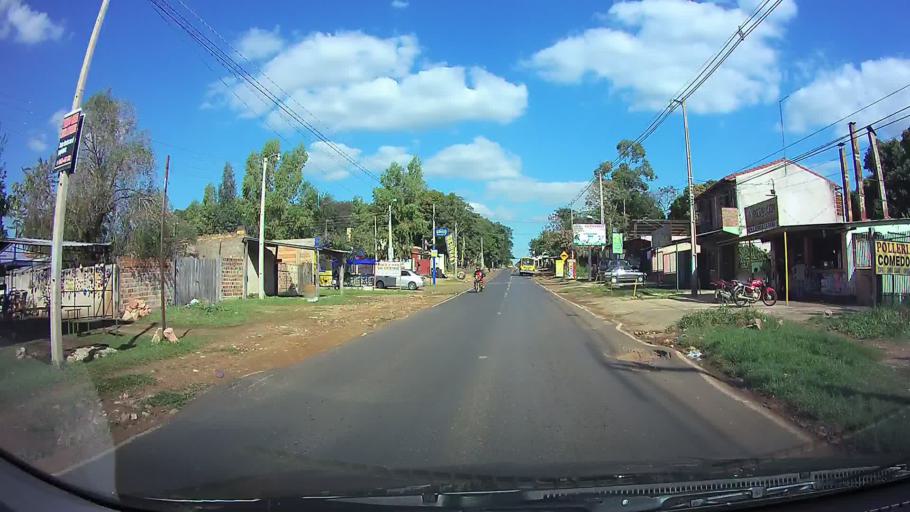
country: PY
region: Central
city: Limpio
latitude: -25.2304
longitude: -57.4761
